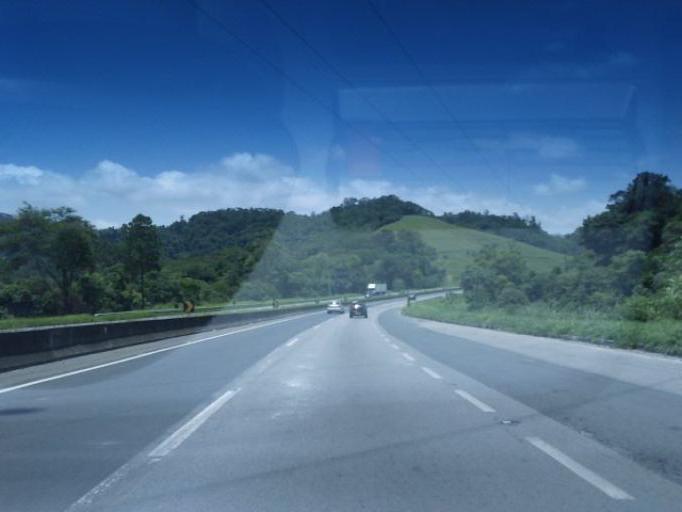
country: BR
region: Sao Paulo
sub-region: Miracatu
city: Miracatu
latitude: -24.2611
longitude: -47.3779
